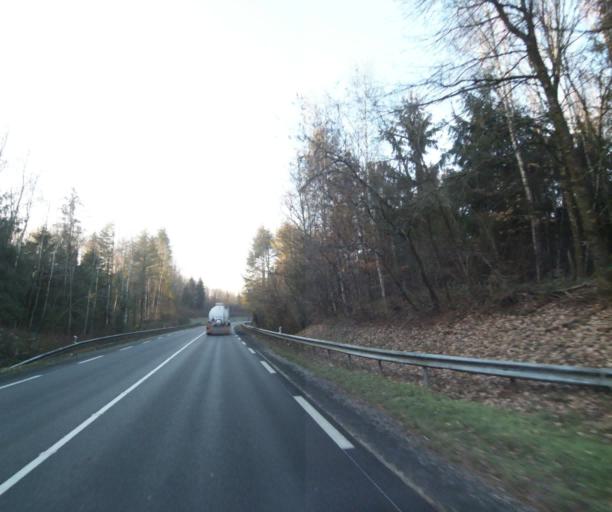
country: FR
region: Champagne-Ardenne
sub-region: Departement de la Haute-Marne
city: Bienville
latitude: 48.5640
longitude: 5.0385
